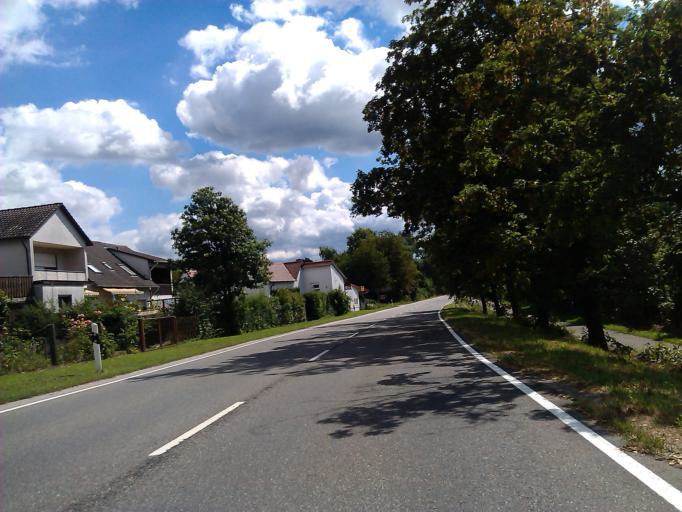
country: DE
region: Rheinland-Pfalz
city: Otterstadt
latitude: 49.3683
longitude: 8.4534
